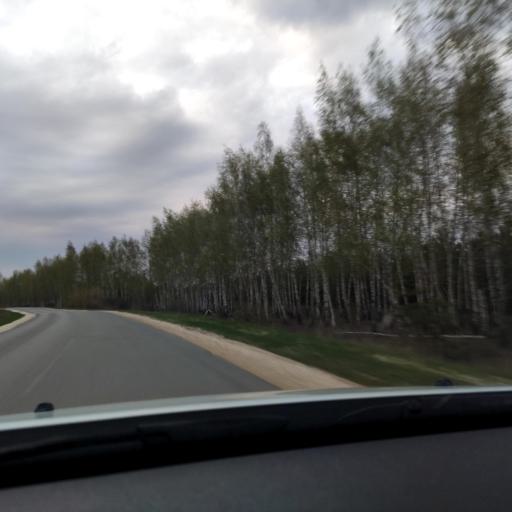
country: RU
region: Lipetsk
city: Donskoye
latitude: 52.6365
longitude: 38.9871
